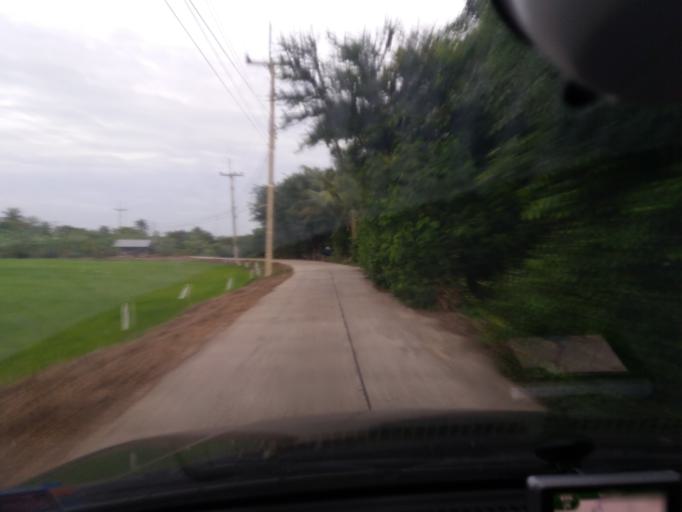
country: TH
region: Suphan Buri
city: Ban Sam Chuk
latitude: 14.7101
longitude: 100.0365
